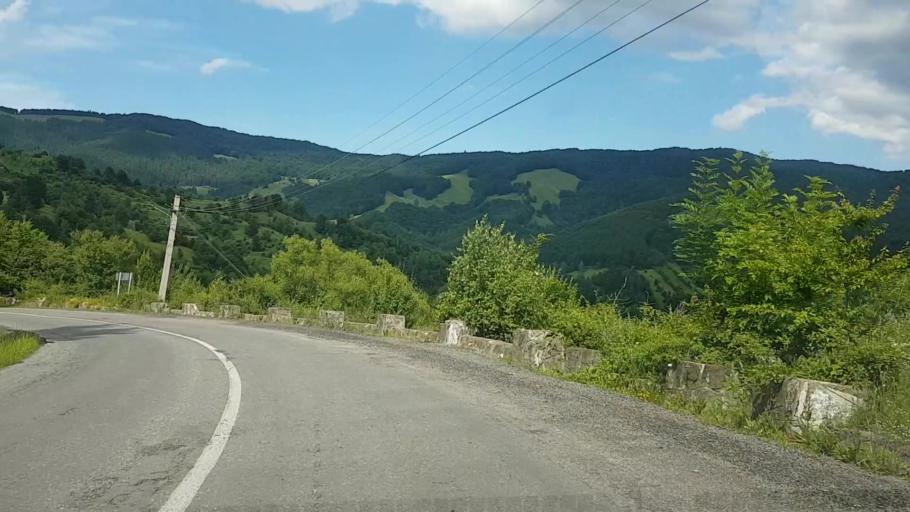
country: RO
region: Neamt
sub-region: Comuna Bicaz
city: Dodeni
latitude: 46.9859
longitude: 26.1069
